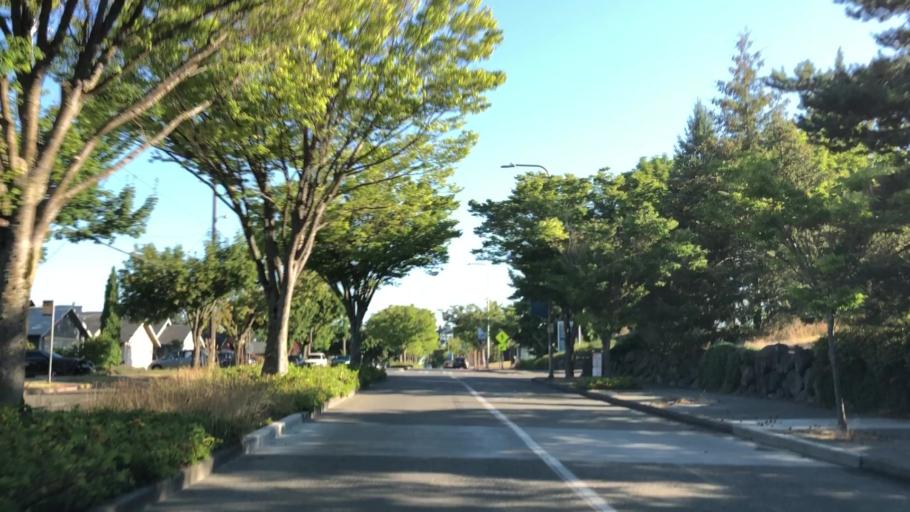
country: US
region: Washington
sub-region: King County
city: White Center
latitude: 47.5483
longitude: -122.3549
